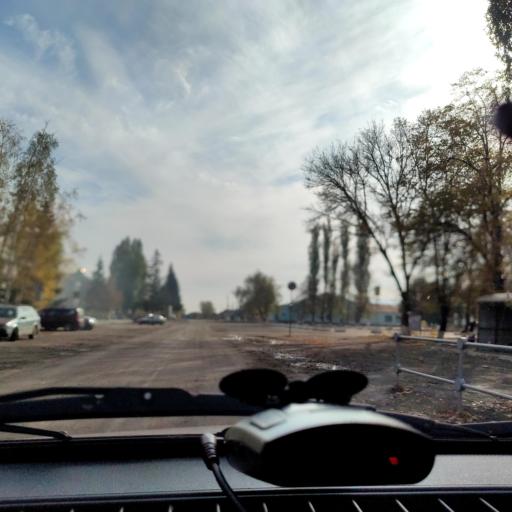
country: RU
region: Voronezj
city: Rossosh'
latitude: 51.2025
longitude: 38.7672
